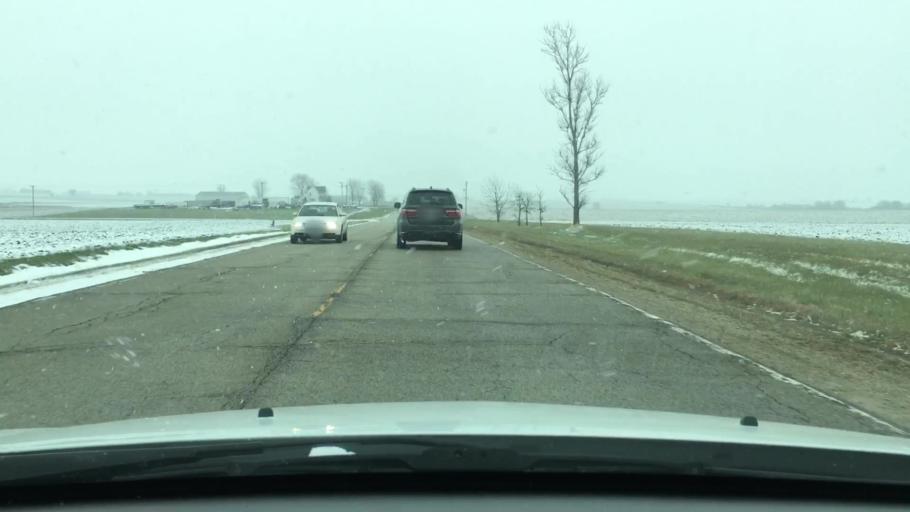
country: US
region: Illinois
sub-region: DeKalb County
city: Malta
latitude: 41.9353
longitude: -88.9442
